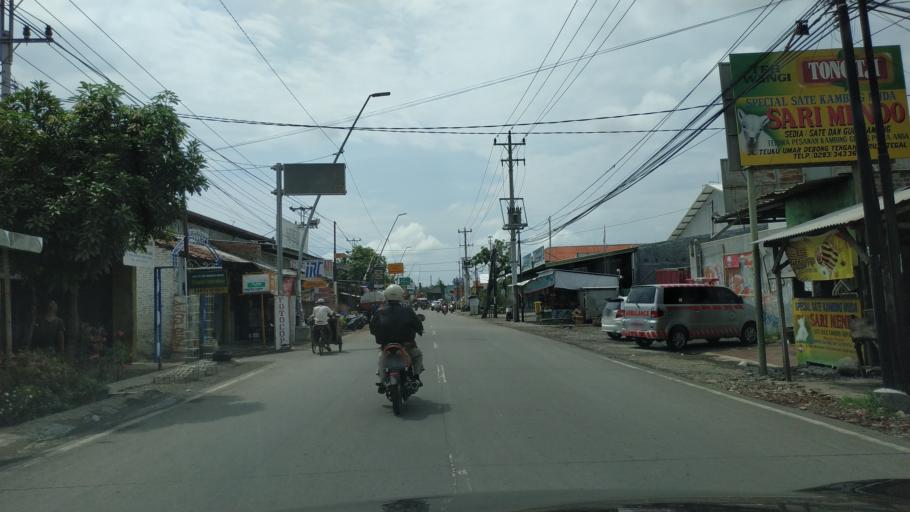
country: ID
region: Central Java
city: Tegal
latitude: -6.8851
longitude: 109.1268
